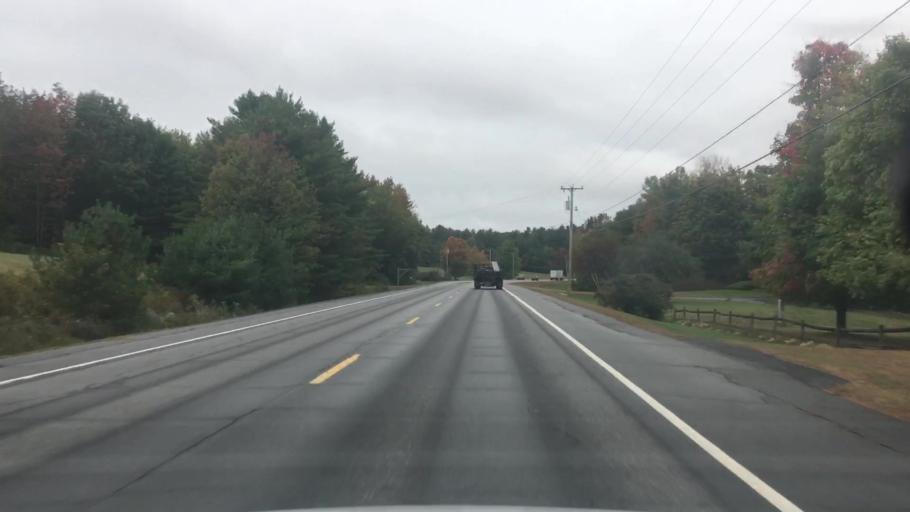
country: US
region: Maine
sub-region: Kennebec County
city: Belgrade
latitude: 44.4322
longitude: -69.8325
